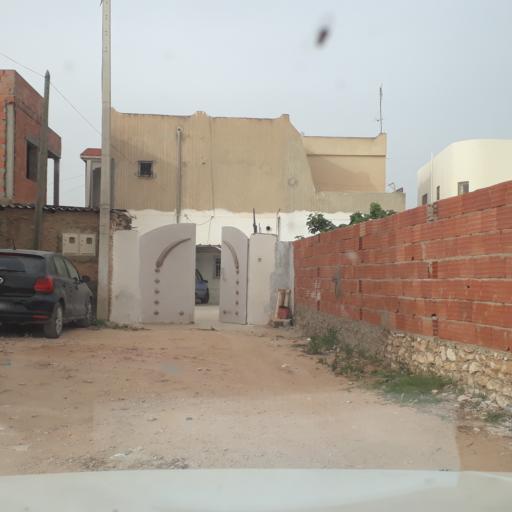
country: TN
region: Safaqis
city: Al Qarmadah
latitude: 34.8181
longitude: 10.7739
